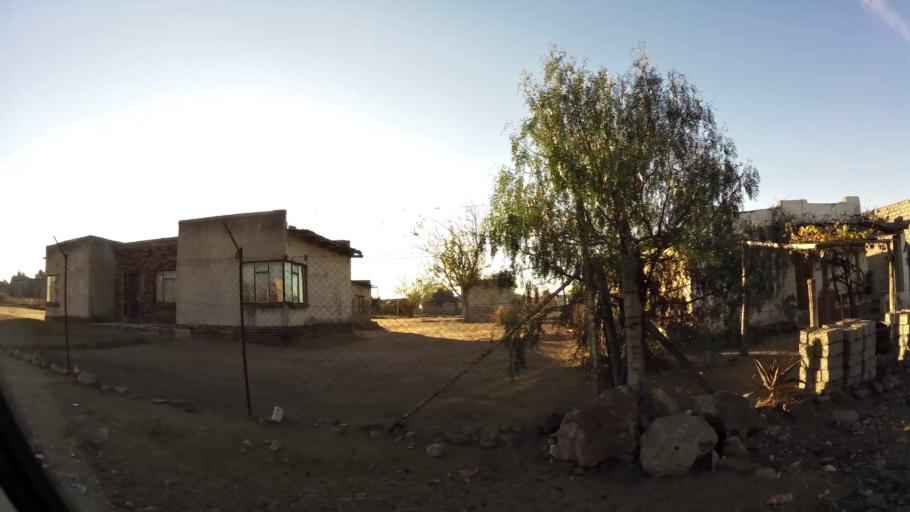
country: ZA
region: Limpopo
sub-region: Capricorn District Municipality
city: Polokwane
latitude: -23.8189
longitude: 29.3788
